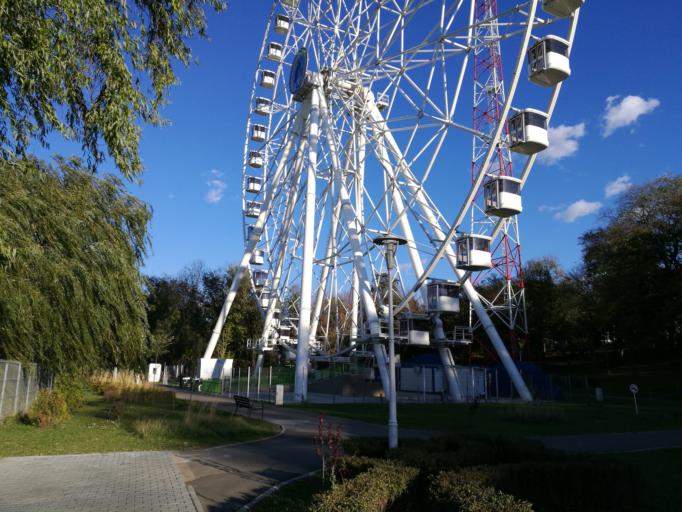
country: RO
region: Bucuresti
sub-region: Municipiul Bucuresti
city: Bucharest
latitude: 44.4663
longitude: 26.1255
